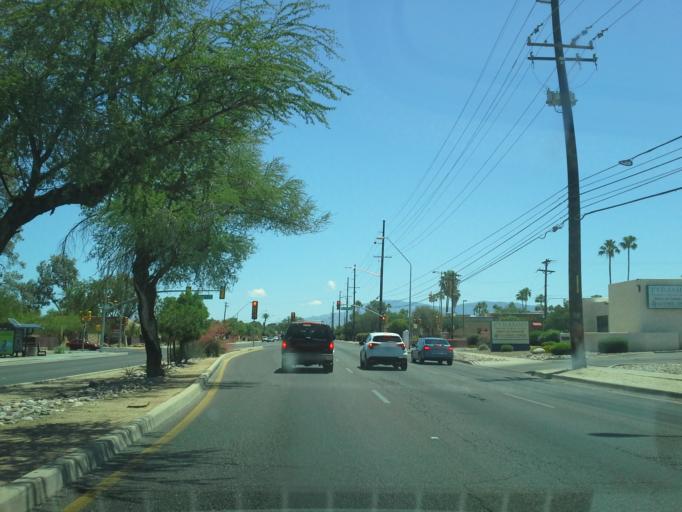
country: US
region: Arizona
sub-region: Pima County
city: Tucson
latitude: 32.2506
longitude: -110.8807
